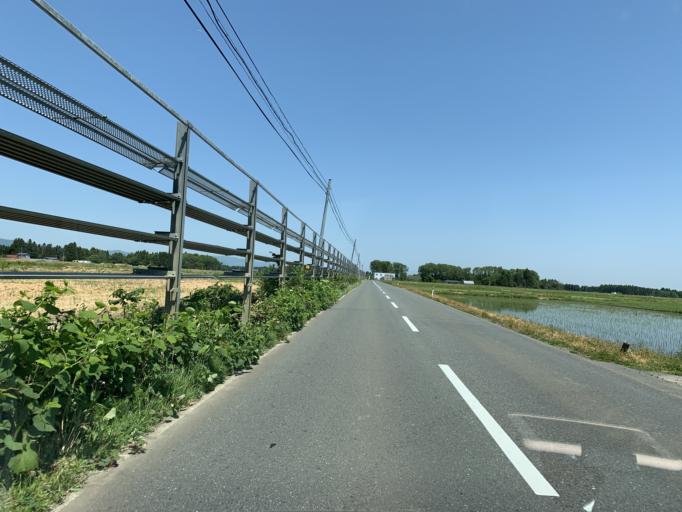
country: JP
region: Iwate
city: Kitakami
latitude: 39.2560
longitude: 141.0648
